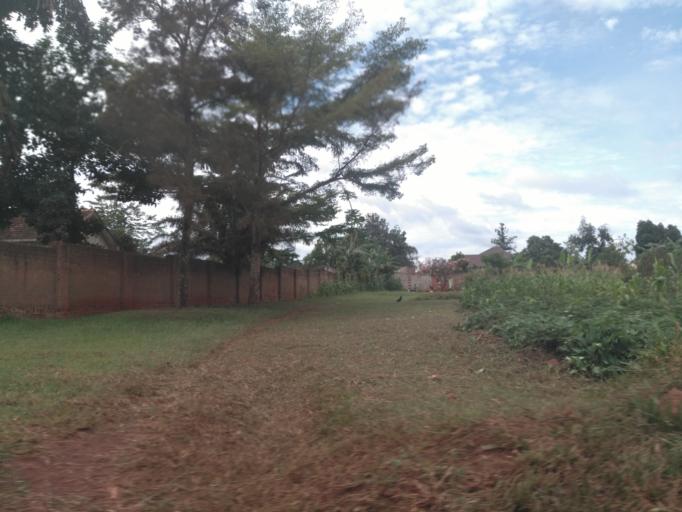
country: UG
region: Eastern Region
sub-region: Jinja District
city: Jinja
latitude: 0.4284
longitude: 33.1901
